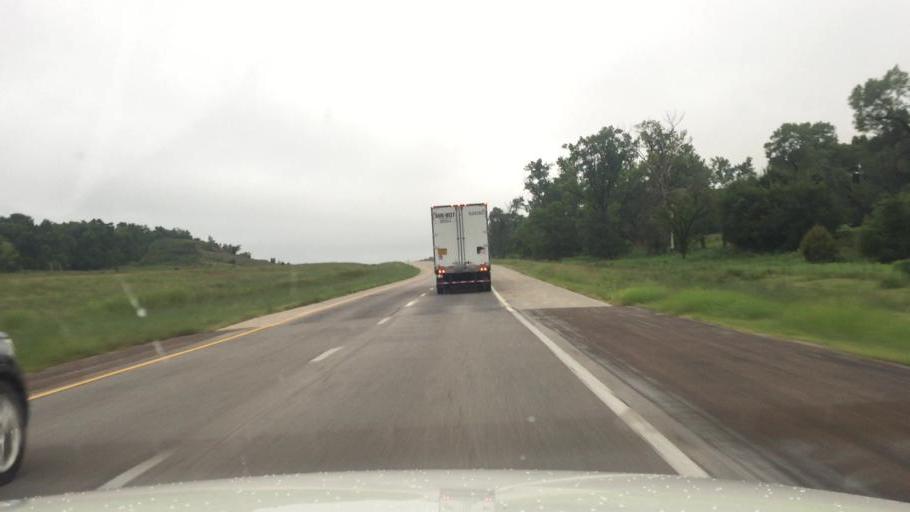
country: US
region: Kansas
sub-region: Montgomery County
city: Cherryvale
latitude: 37.2194
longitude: -95.5856
